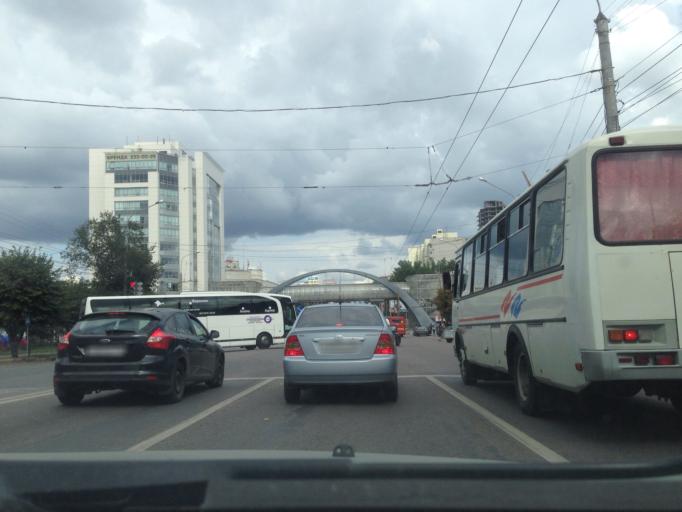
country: RU
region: Voronezj
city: Voronezh
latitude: 51.6918
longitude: 39.1833
